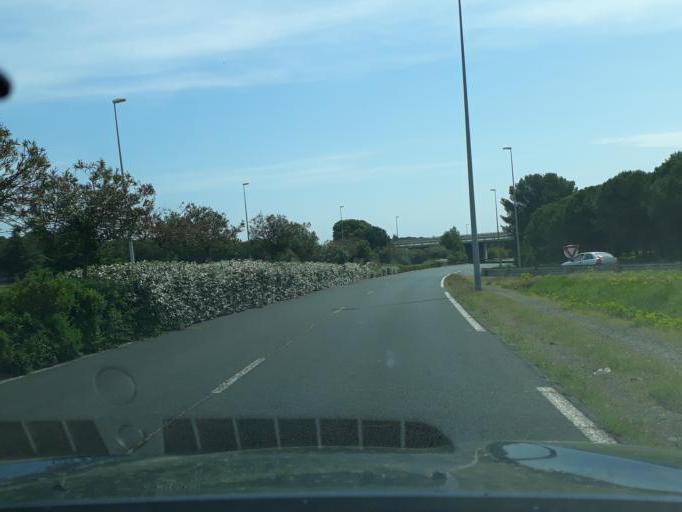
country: FR
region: Languedoc-Roussillon
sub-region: Departement de l'Herault
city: Le Cap d'Agde
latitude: 43.2947
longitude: 3.5013
